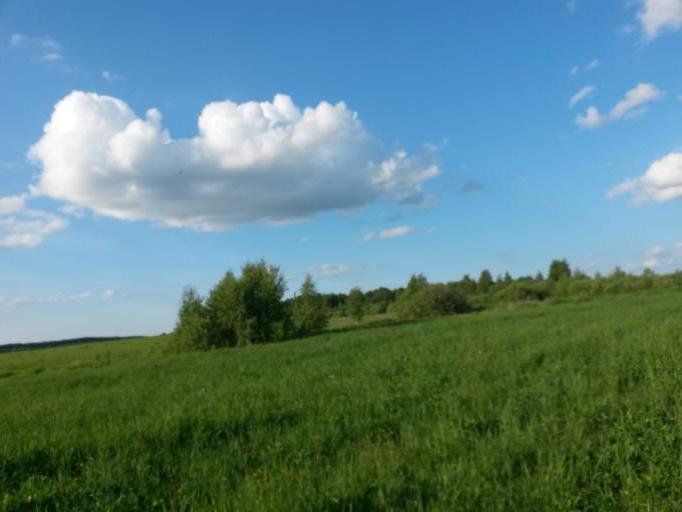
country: RU
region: Jaroslavl
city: Burmakino
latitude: 57.3634
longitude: 40.1990
